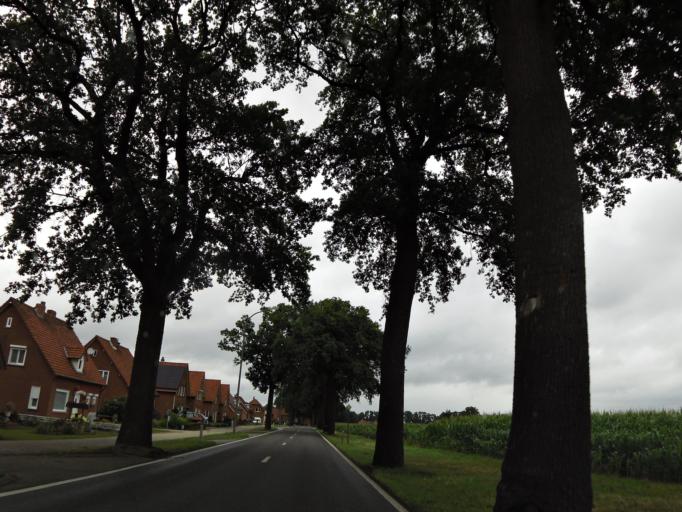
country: BE
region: Flanders
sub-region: Provincie Limburg
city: Bree
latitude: 51.1244
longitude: 5.5918
